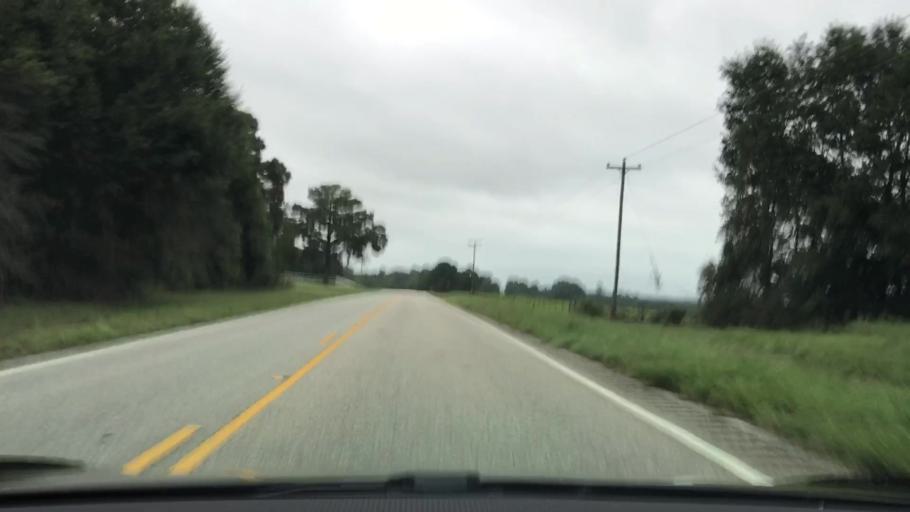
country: US
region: Alabama
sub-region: Coffee County
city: Elba
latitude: 31.3581
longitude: -86.1195
